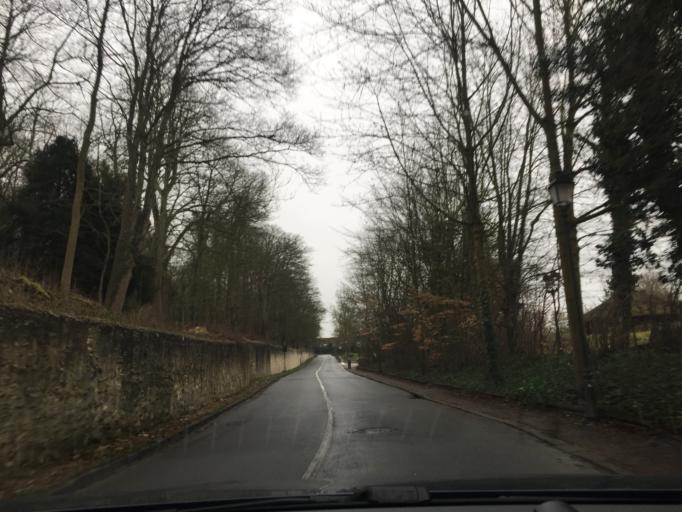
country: FR
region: Ile-de-France
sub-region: Departement de Seine-et-Marne
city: Coupvray
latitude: 48.8906
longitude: 2.7927
